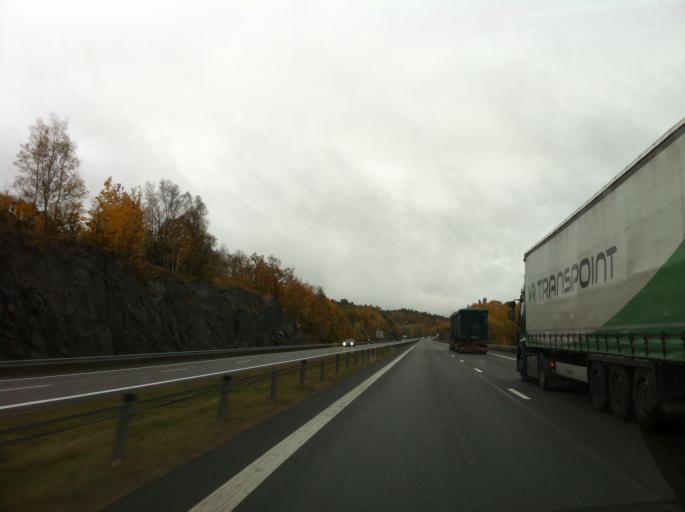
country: SE
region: Joenkoeping
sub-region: Jonkopings Kommun
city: Graenna
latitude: 58.0381
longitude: 14.4960
